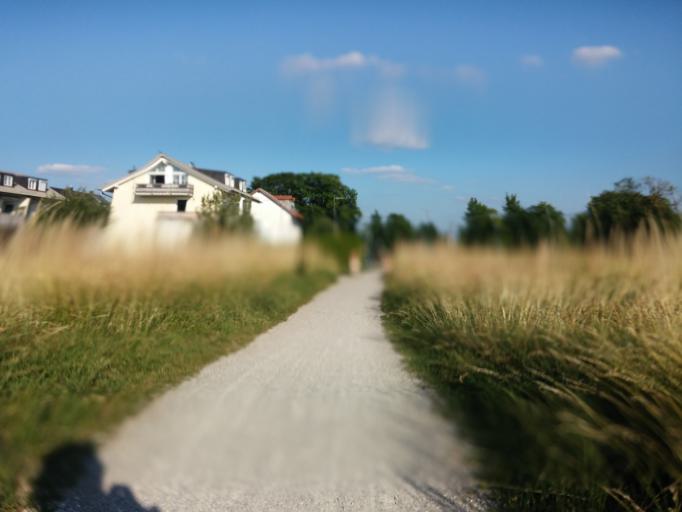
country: DE
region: Bavaria
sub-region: Upper Bavaria
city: Neubiberg
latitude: 48.1278
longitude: 11.6623
